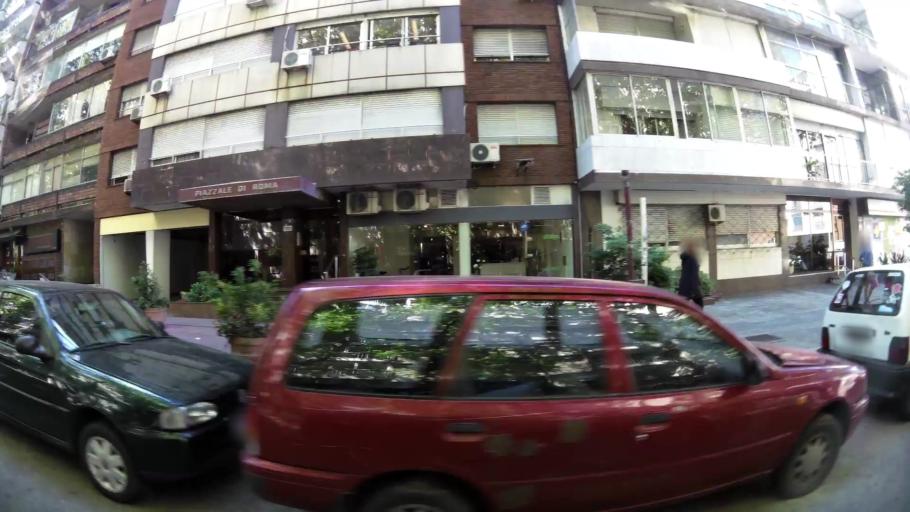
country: UY
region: Montevideo
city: Montevideo
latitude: -34.9114
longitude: -56.1464
